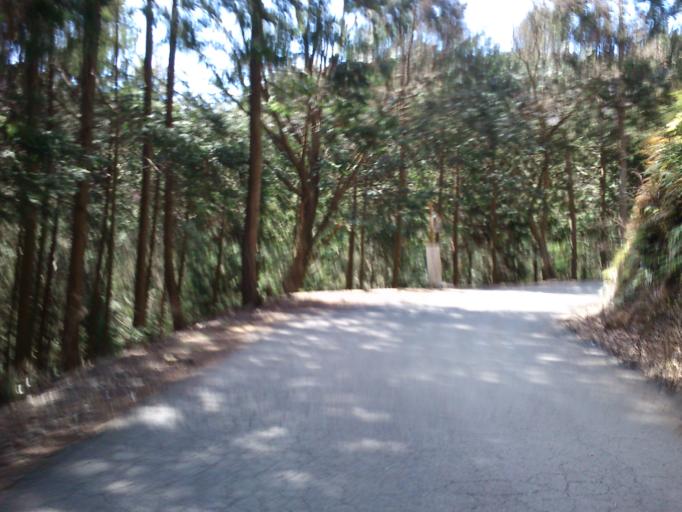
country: JP
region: Shiga Prefecture
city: Otsu-shi
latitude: 34.9507
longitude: 135.8433
